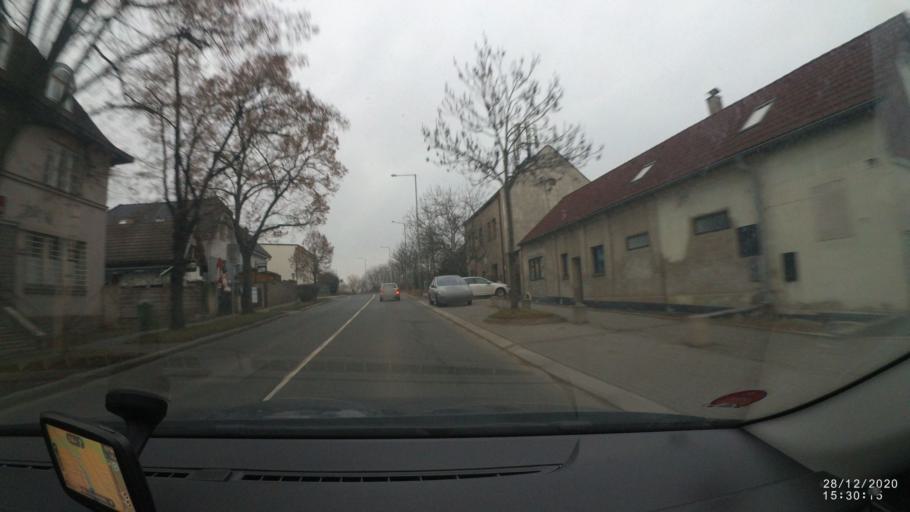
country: CZ
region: Praha
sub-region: Praha 14
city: Dolni Pocernice
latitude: 50.0865
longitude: 14.5738
